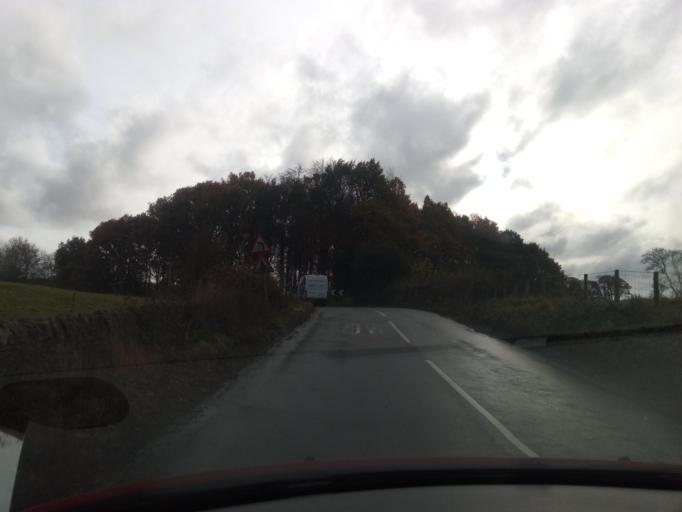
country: GB
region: England
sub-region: Northumberland
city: Birtley
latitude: 55.0576
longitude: -2.1924
